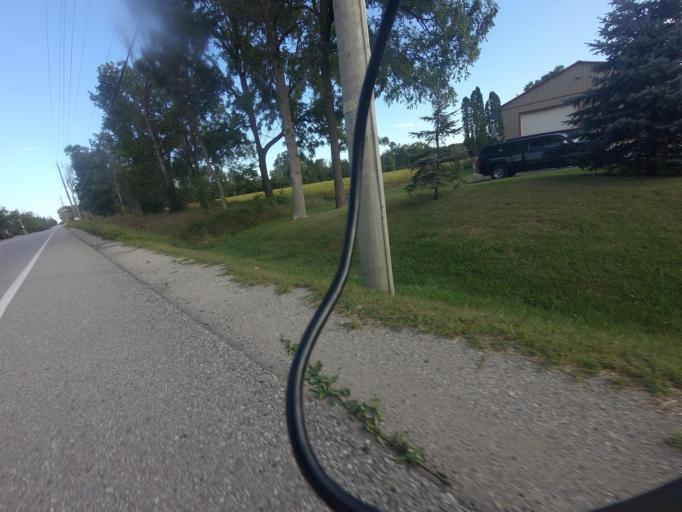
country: CA
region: Ontario
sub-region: Wellington County
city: Guelph
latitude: 43.5755
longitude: -80.3294
